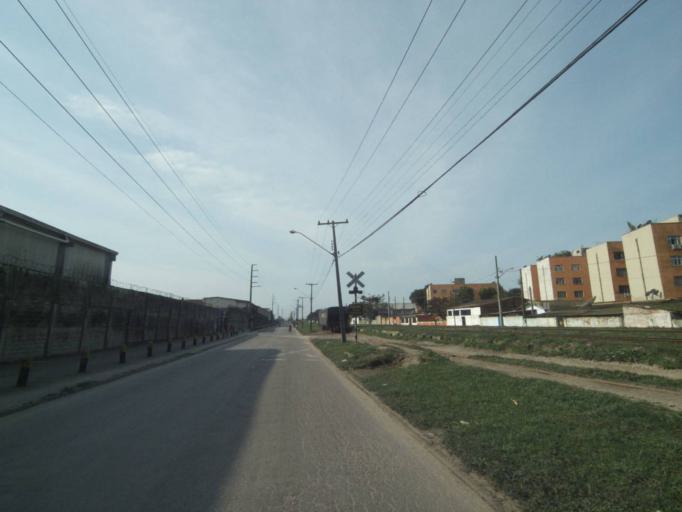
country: BR
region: Parana
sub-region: Paranagua
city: Paranagua
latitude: -25.5327
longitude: -48.5320
